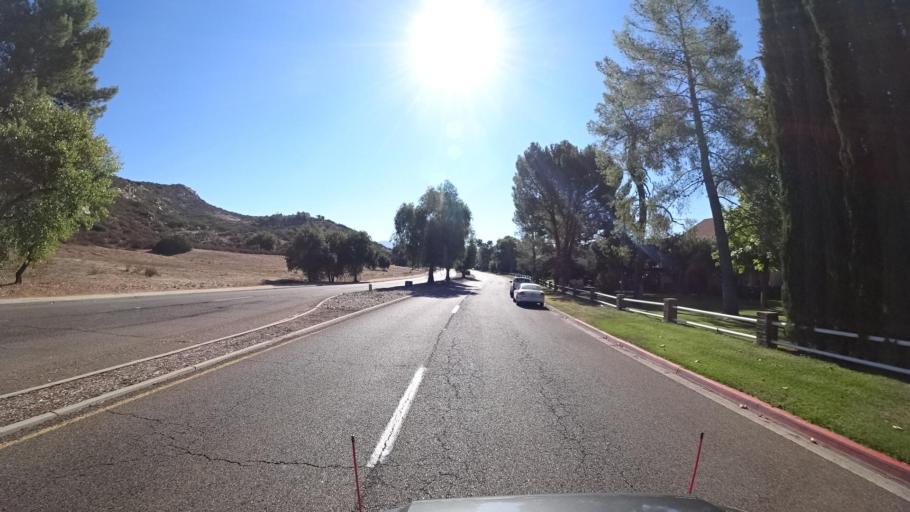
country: US
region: California
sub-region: San Diego County
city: San Diego Country Estates
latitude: 33.0048
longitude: -116.8124
